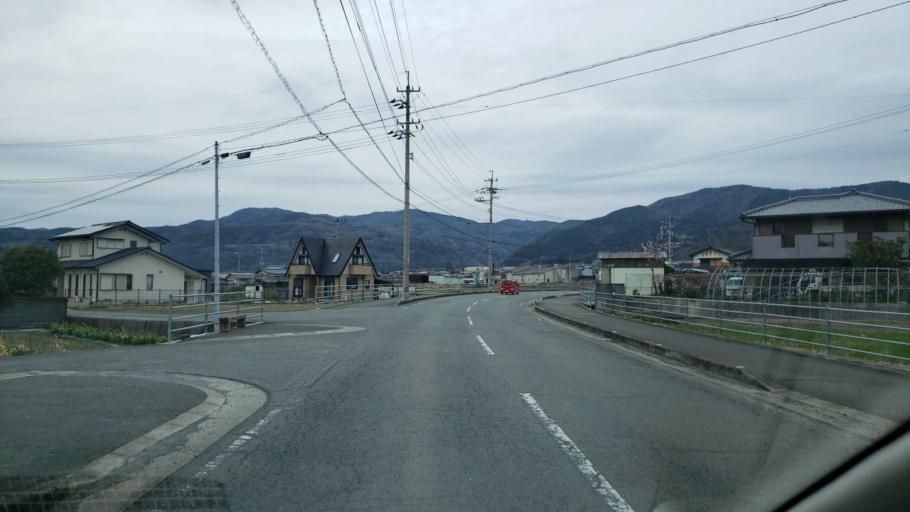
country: JP
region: Tokushima
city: Kamojimacho-jogejima
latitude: 34.1083
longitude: 134.3405
